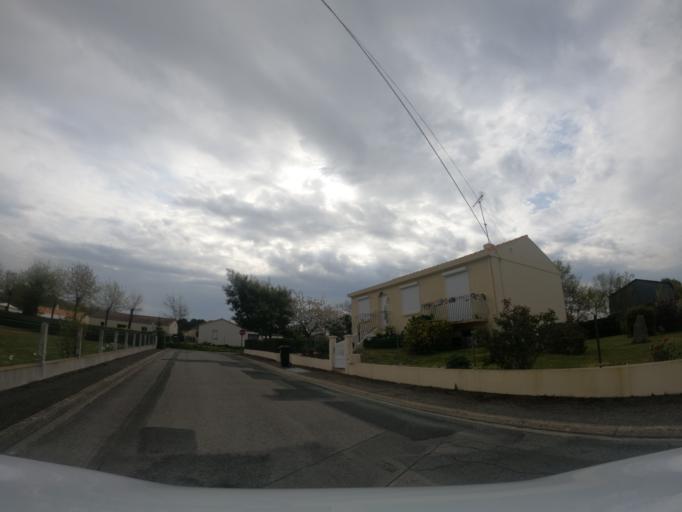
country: FR
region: Pays de la Loire
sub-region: Departement de la Vendee
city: Le Champ-Saint-Pere
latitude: 46.5094
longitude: -1.3396
